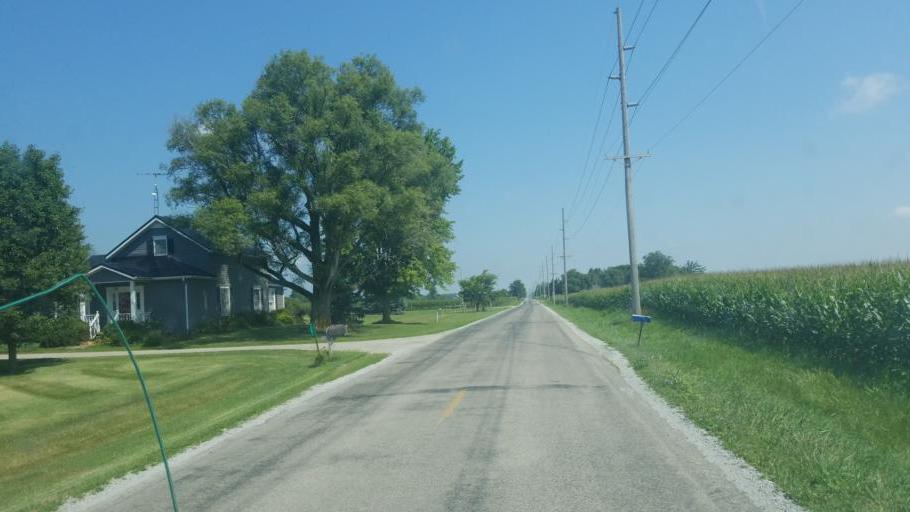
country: US
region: Ohio
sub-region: Hardin County
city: Kenton
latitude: 40.6869
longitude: -83.6540
